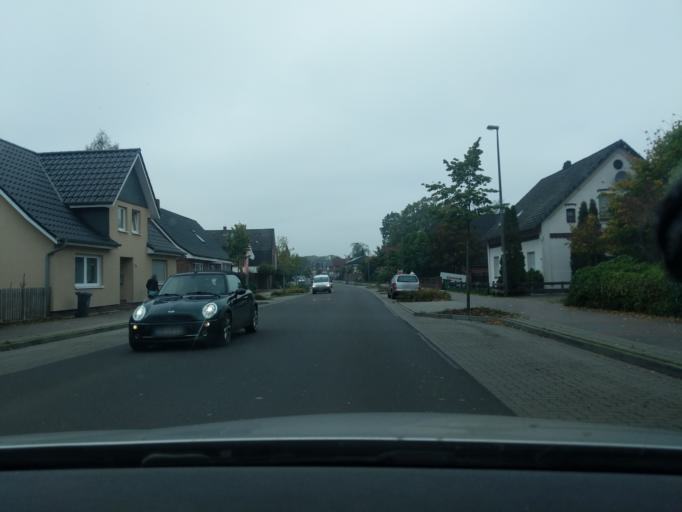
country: DE
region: Lower Saxony
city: Hemmoor
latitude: 53.6849
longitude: 9.1753
